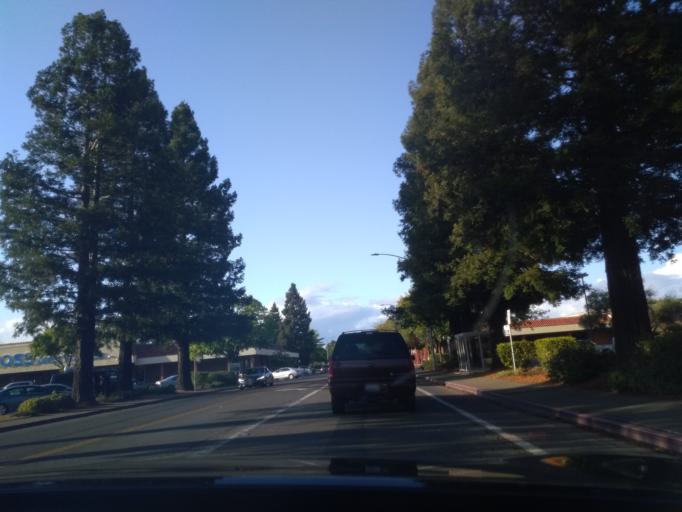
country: US
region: California
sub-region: Mendocino County
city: Ukiah
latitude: 39.1523
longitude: -123.1991
